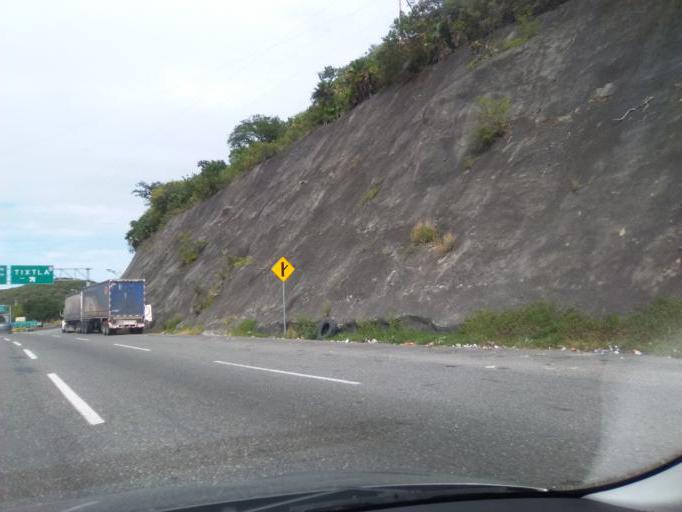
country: MX
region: Guerrero
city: Chilpancingo de los Bravos
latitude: 17.6009
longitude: -99.5191
